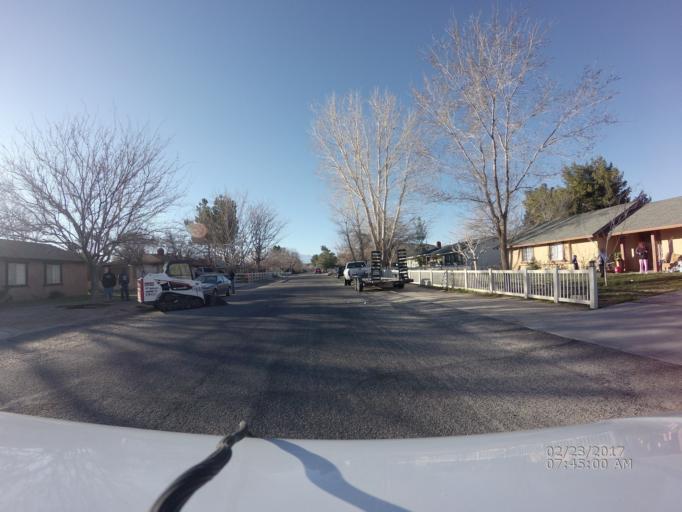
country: US
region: California
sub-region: Los Angeles County
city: Lake Los Angeles
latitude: 34.6139
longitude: -117.8121
